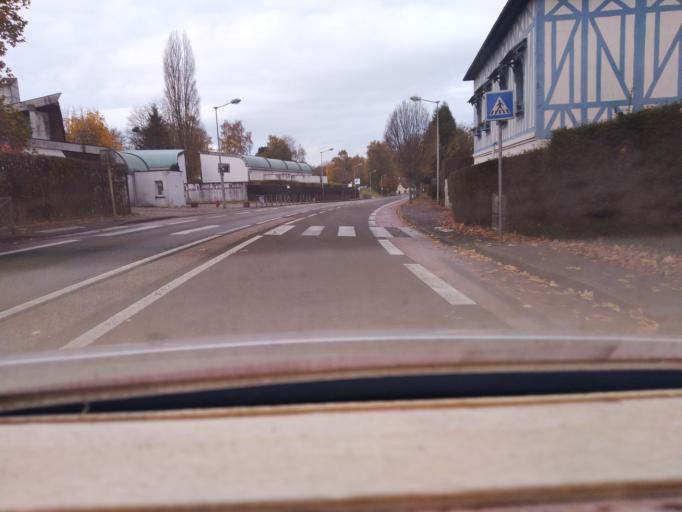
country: FR
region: Haute-Normandie
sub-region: Departement de la Seine-Maritime
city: Canteleu
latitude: 49.4430
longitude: 1.0192
